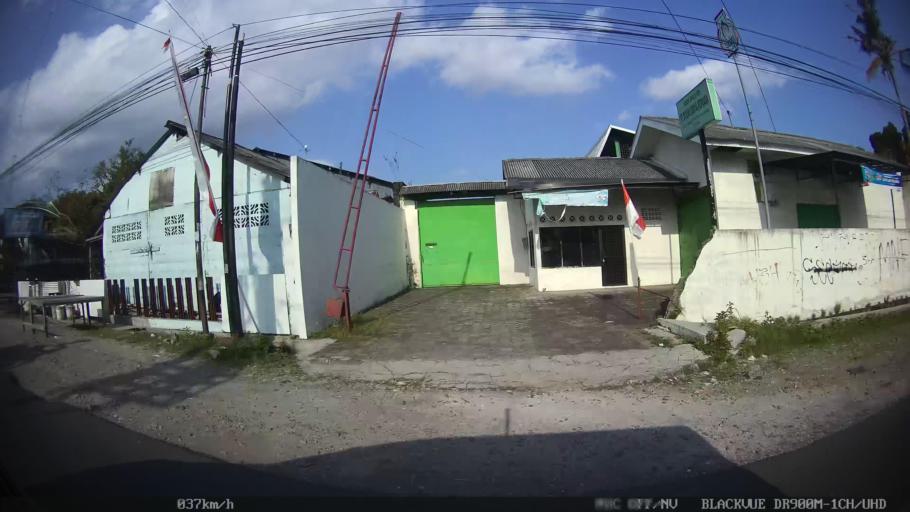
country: ID
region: Daerah Istimewa Yogyakarta
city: Yogyakarta
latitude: -7.7828
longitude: 110.3499
